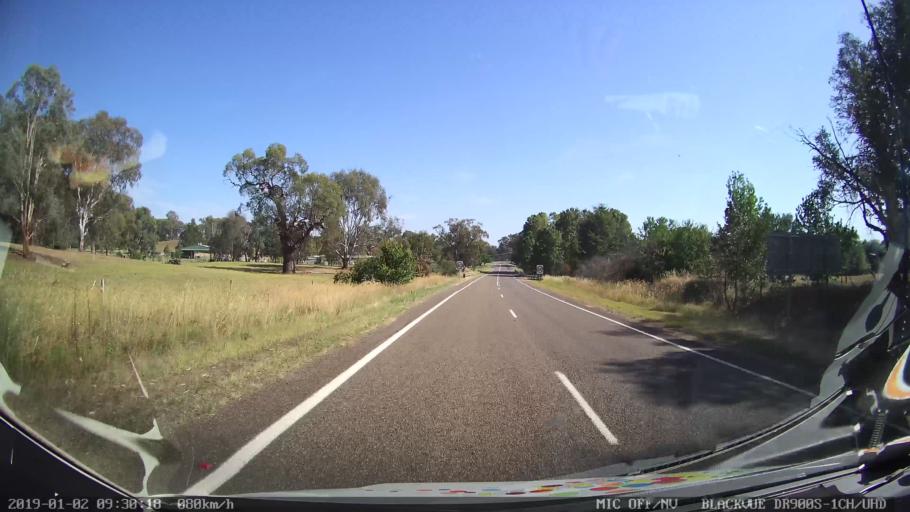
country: AU
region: New South Wales
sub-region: Tumut Shire
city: Tumut
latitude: -35.3281
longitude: 148.2376
